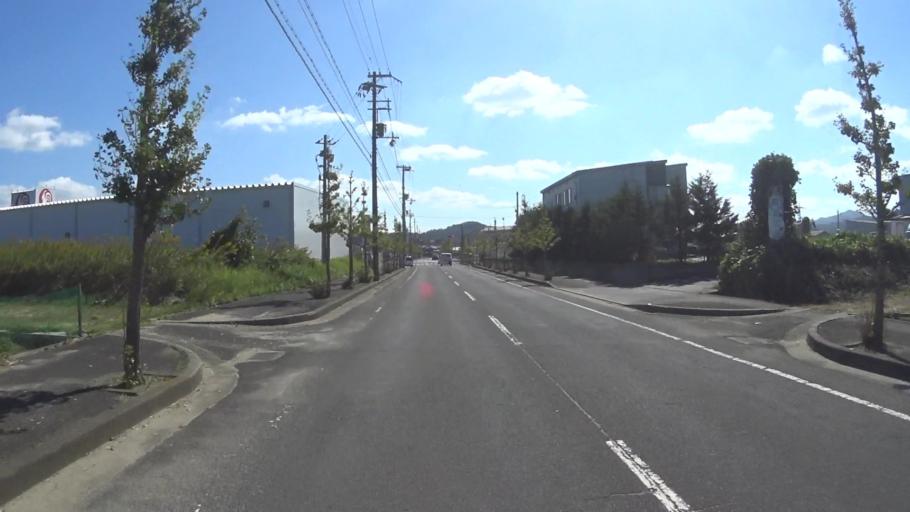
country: JP
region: Kyoto
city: Miyazu
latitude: 35.6803
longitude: 135.0223
